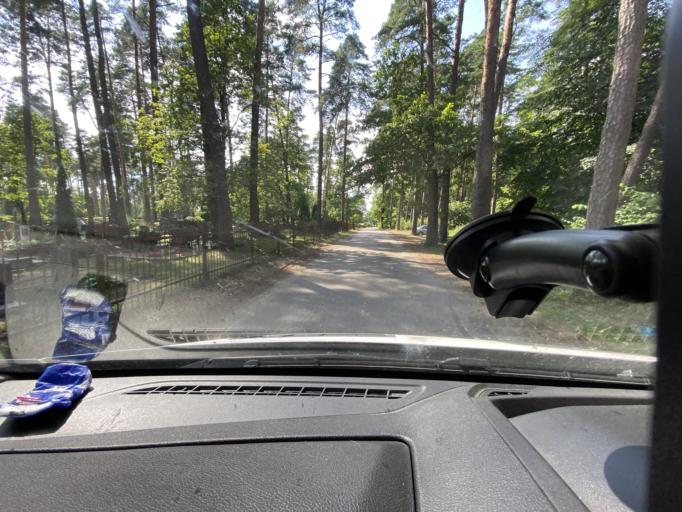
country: LT
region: Kauno apskritis
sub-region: Kauno rajonas
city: Karmelava
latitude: 54.9743
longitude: 24.0485
